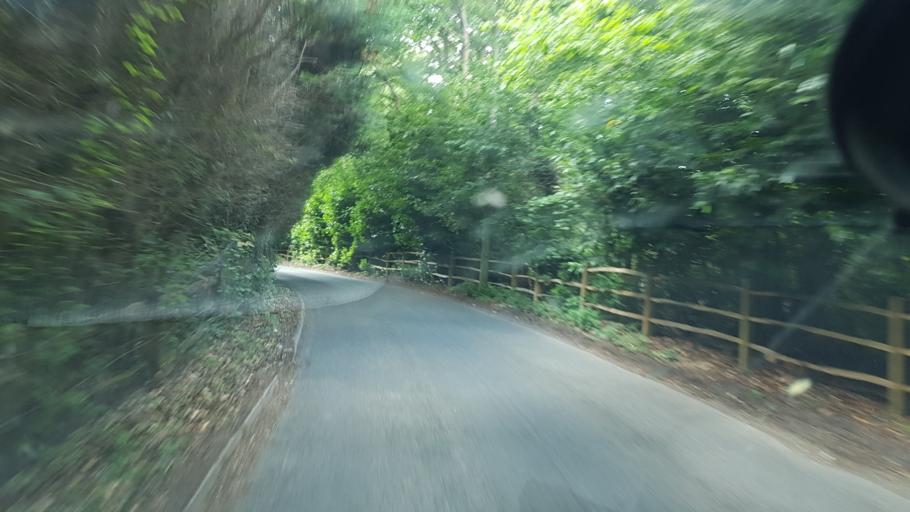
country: GB
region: England
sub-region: West Sussex
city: Maidenbower
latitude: 51.0661
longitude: -0.1572
